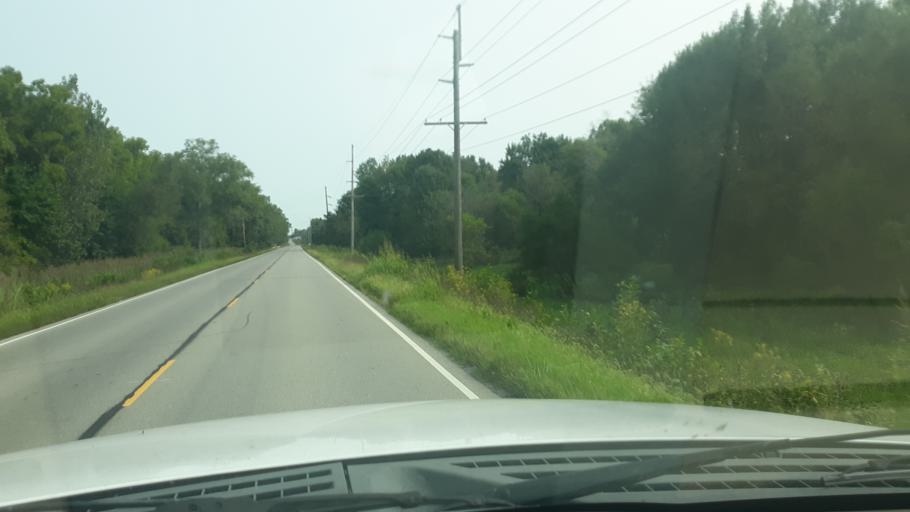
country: US
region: Illinois
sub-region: White County
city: Norris City
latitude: 37.9395
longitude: -88.3436
